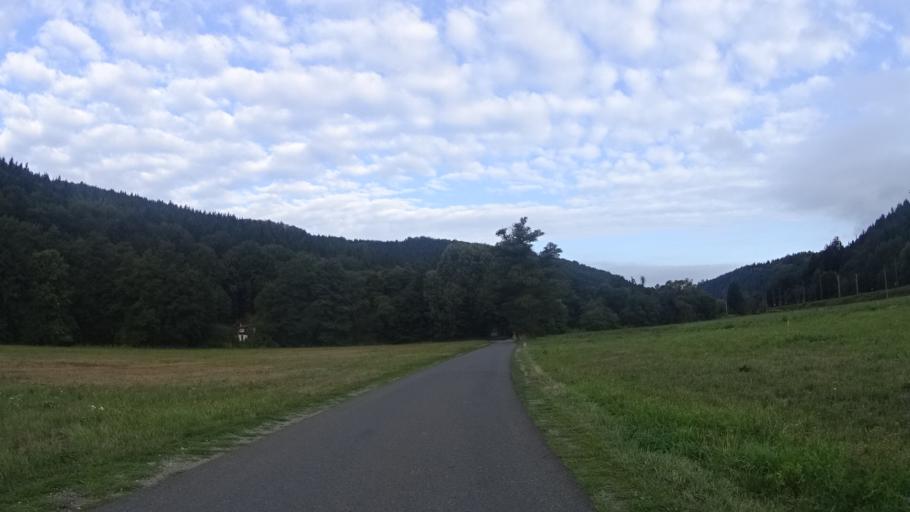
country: CZ
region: Olomoucky
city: Zabreh
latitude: 49.8662
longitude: 16.7941
